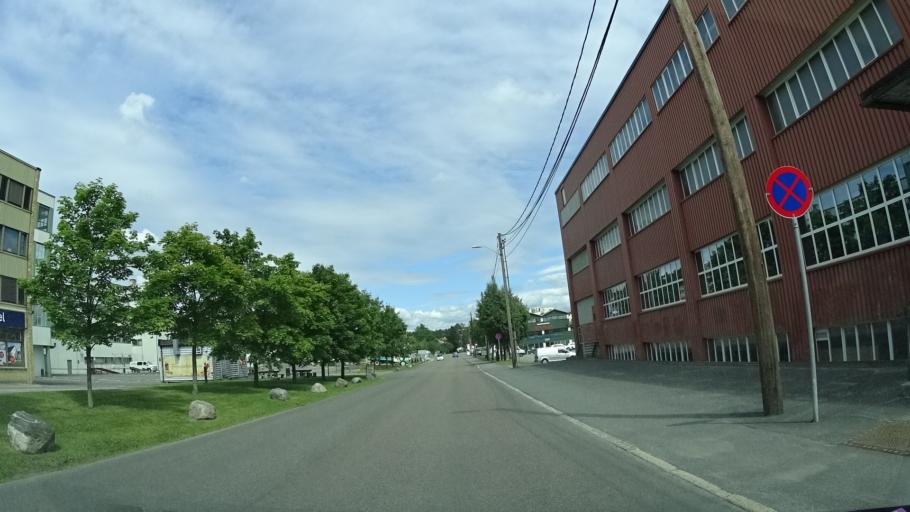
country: NO
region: Oslo
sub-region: Oslo
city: Oslo
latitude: 59.9644
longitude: 10.7709
